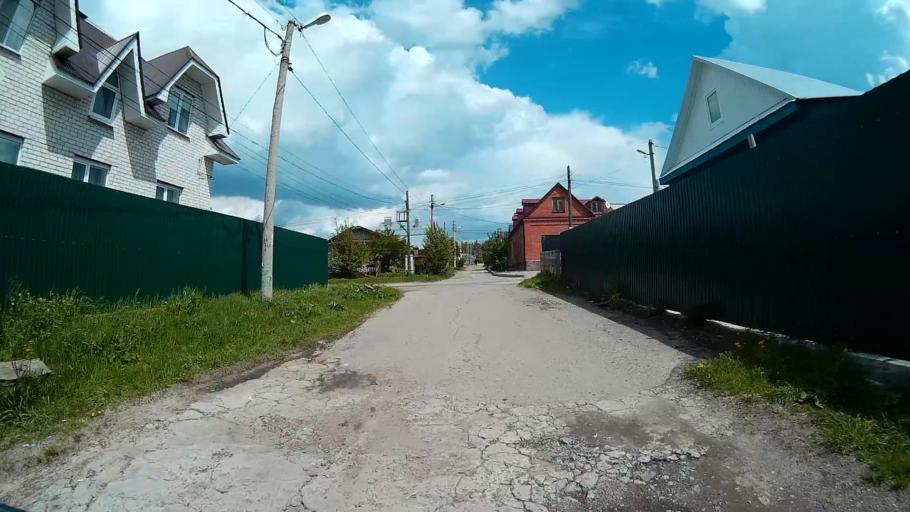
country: RU
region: Ulyanovsk
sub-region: Ulyanovskiy Rayon
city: Ulyanovsk
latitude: 54.3445
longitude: 48.3651
